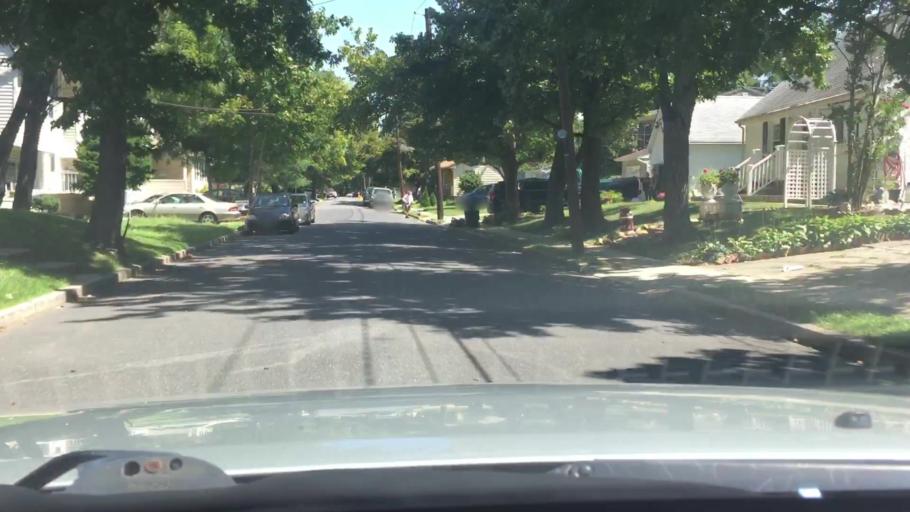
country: US
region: New Jersey
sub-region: Middlesex County
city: South River
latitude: 40.4545
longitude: -74.3969
